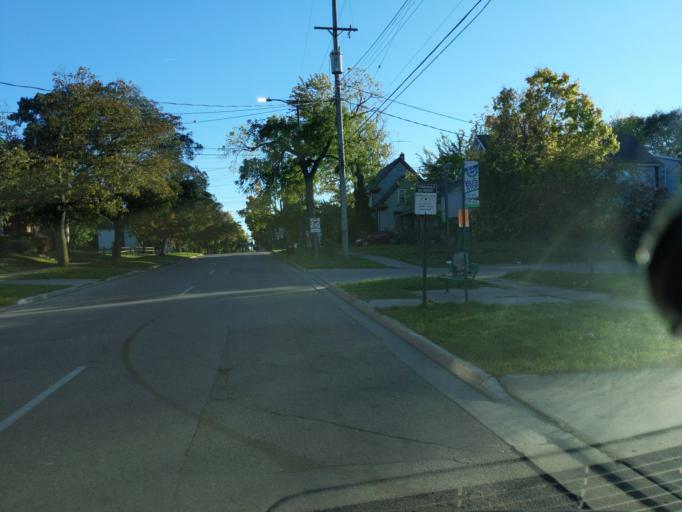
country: US
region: Michigan
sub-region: Ingham County
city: Lansing
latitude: 42.7406
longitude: -84.5600
